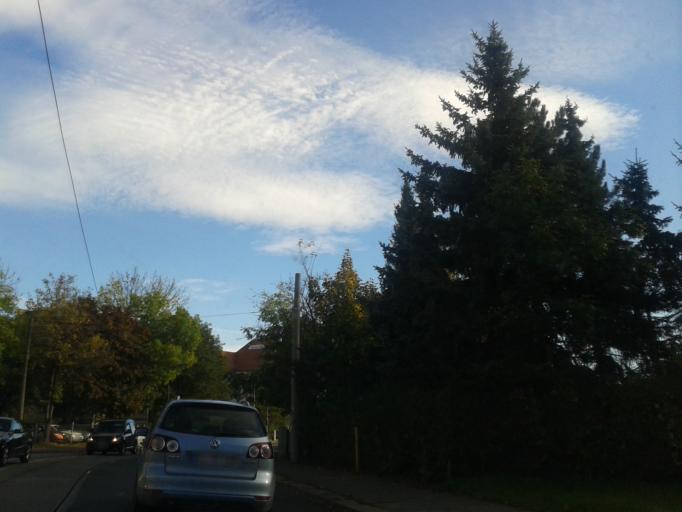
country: DE
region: Saxony
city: Radebeul
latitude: 51.0587
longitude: 13.6843
